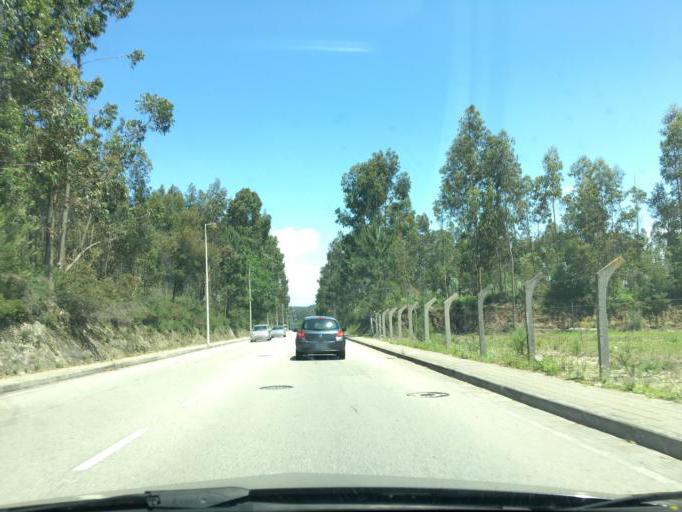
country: PT
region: Porto
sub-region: Maia
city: Anta
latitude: 41.2657
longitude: -8.6230
